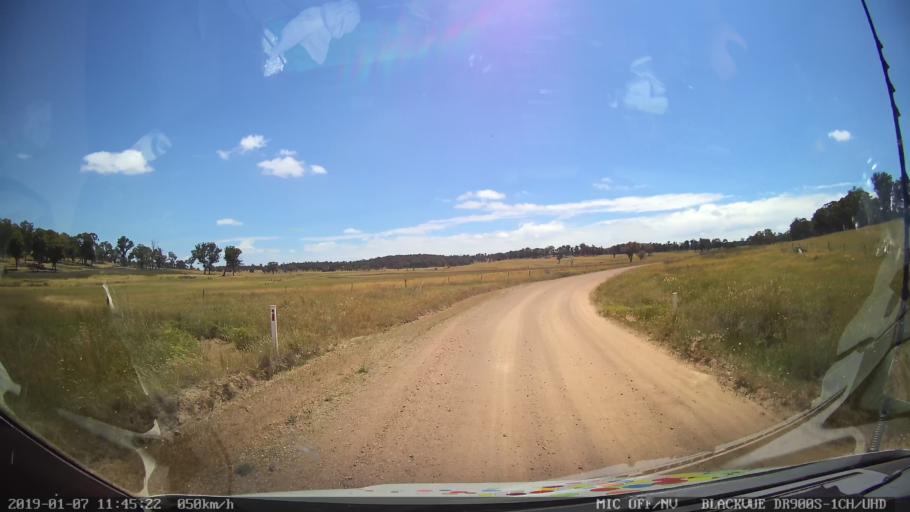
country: AU
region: New South Wales
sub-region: Guyra
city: Guyra
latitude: -30.3464
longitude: 151.6050
